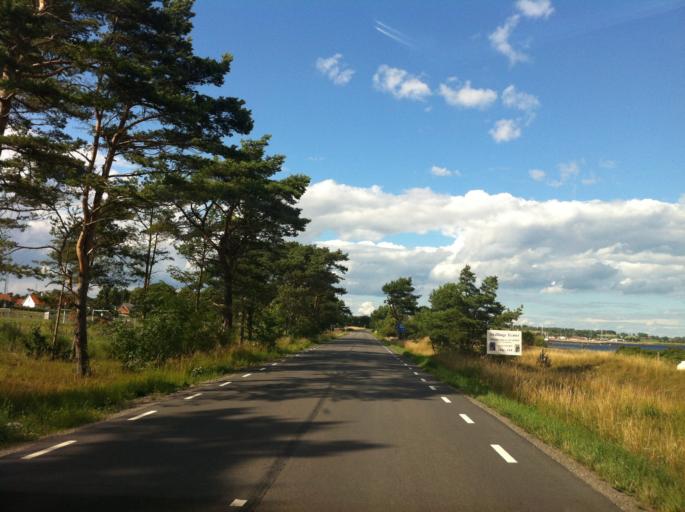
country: SE
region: Skane
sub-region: Simrishamns Kommun
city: Simrishamn
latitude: 55.4550
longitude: 14.2686
